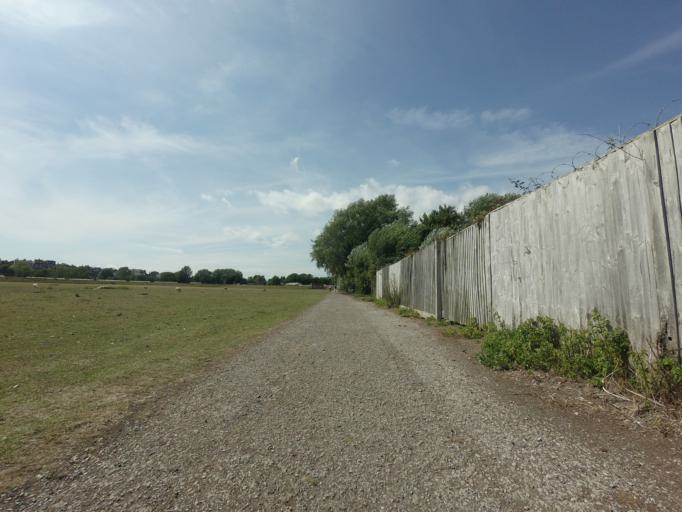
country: GB
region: England
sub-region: East Sussex
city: Rye
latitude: 50.9519
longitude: 0.7426
